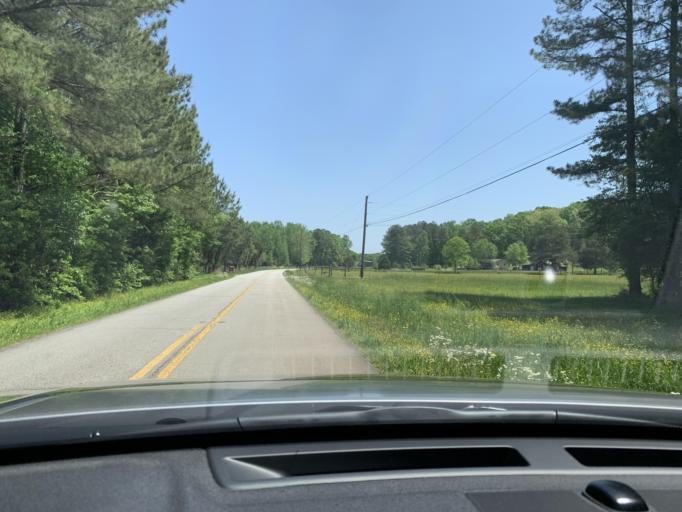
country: US
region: Georgia
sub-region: Polk County
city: Cedartown
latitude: 34.0772
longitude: -85.1584
